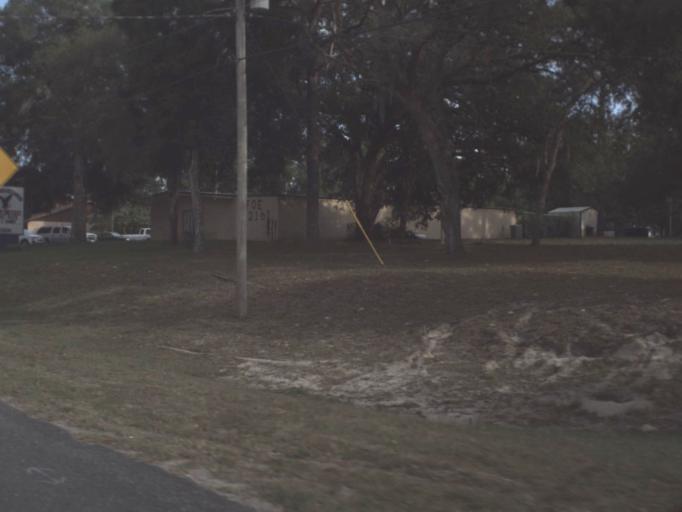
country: US
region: Florida
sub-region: Marion County
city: Silver Springs Shores
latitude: 29.1794
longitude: -81.8841
